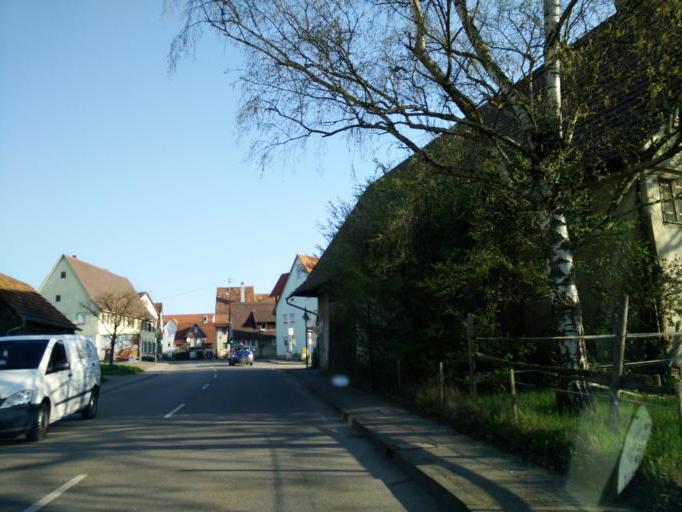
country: DE
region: Baden-Wuerttemberg
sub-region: Regierungsbezirk Stuttgart
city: Herrenberg
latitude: 48.6063
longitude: 8.8596
